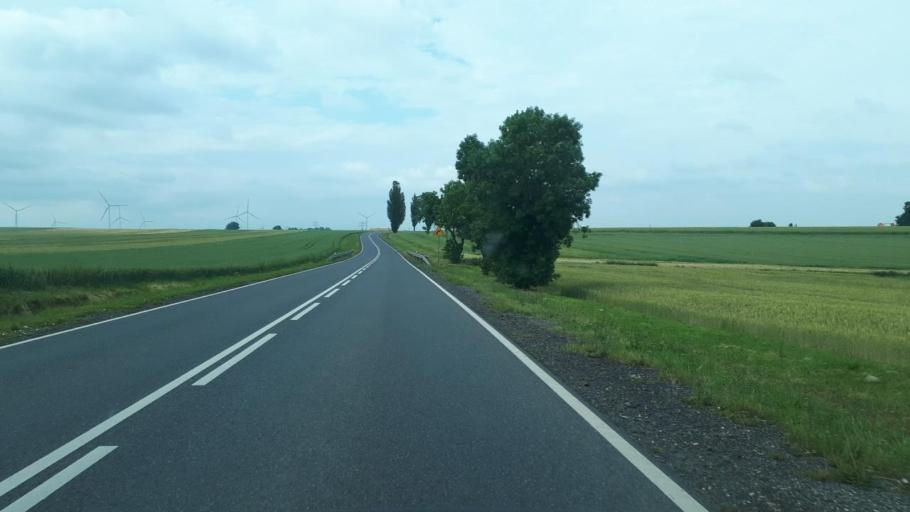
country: PL
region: Silesian Voivodeship
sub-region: Powiat gliwicki
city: Wielowies
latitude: 50.4819
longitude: 18.6065
